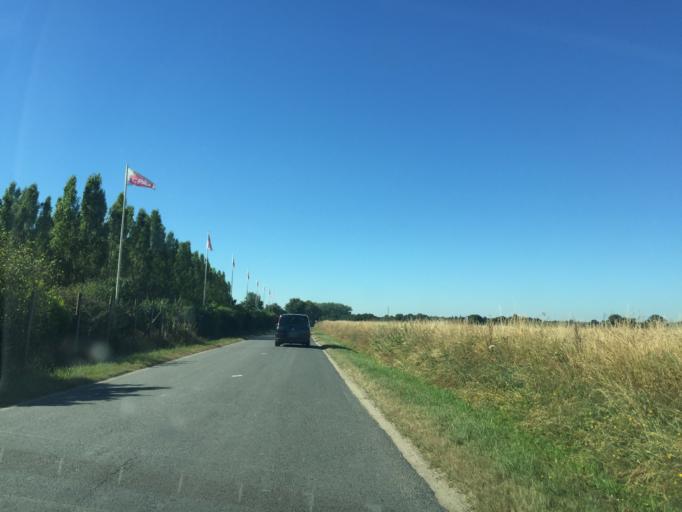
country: FR
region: Auvergne
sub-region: Departement de l'Allier
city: Dompierre-sur-Besbre
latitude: 46.5099
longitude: 3.6225
